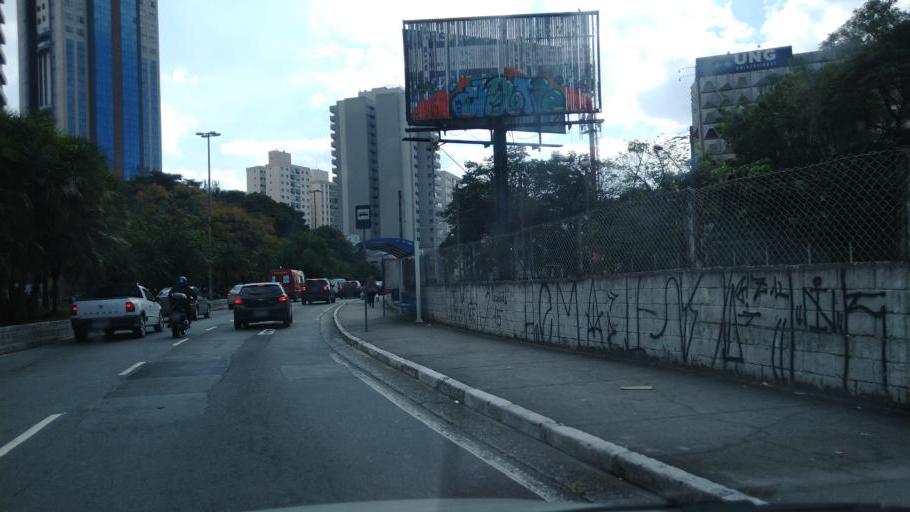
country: BR
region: Sao Paulo
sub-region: Guarulhos
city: Guarulhos
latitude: -23.4713
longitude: -46.5338
